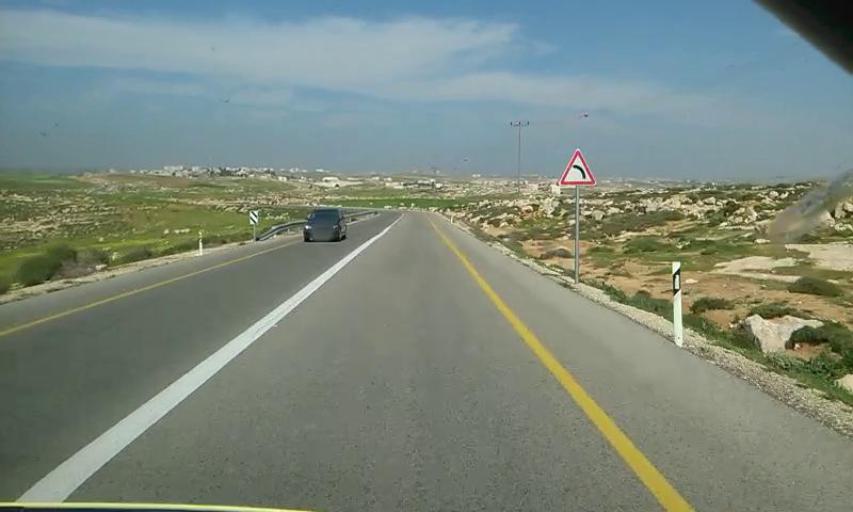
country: PS
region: West Bank
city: As Samu`
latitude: 31.4003
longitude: 35.0316
